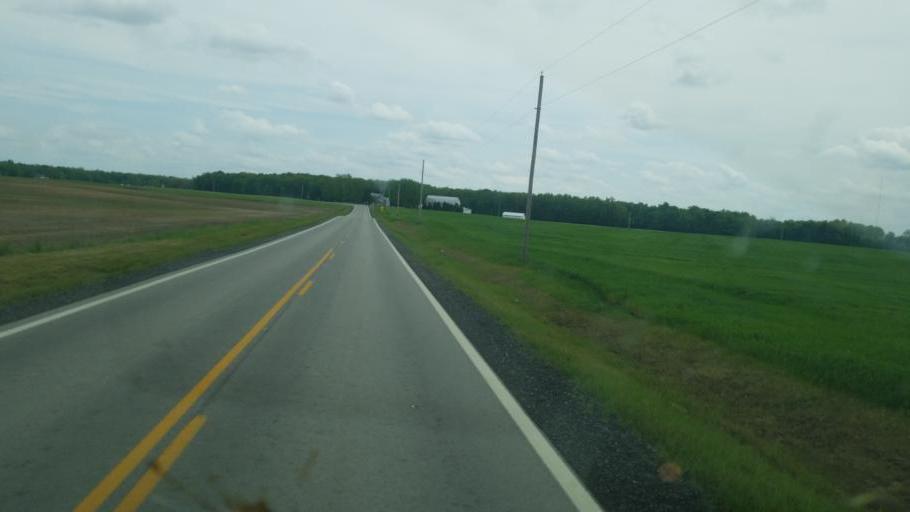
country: US
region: Ohio
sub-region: Crawford County
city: Bucyrus
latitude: 40.9247
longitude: -83.0488
